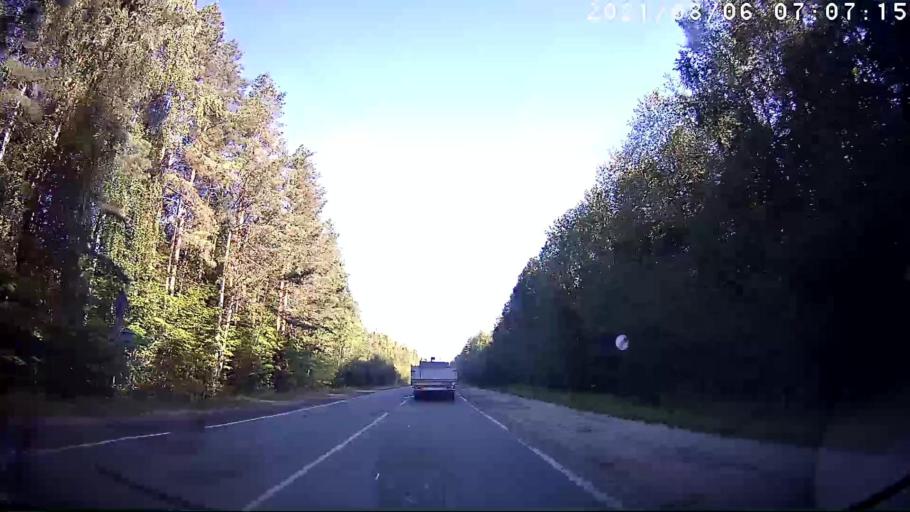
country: RU
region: Mariy-El
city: Yoshkar-Ola
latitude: 56.5621
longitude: 47.9799
